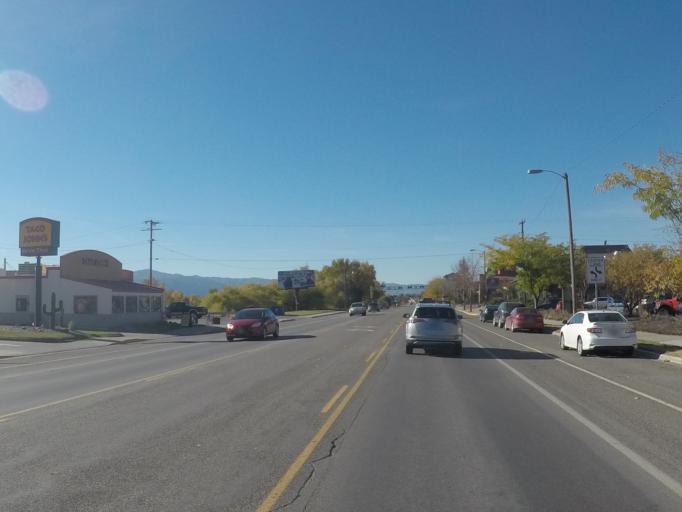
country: US
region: Montana
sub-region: Missoula County
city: Missoula
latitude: 46.8746
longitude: -114.0024
